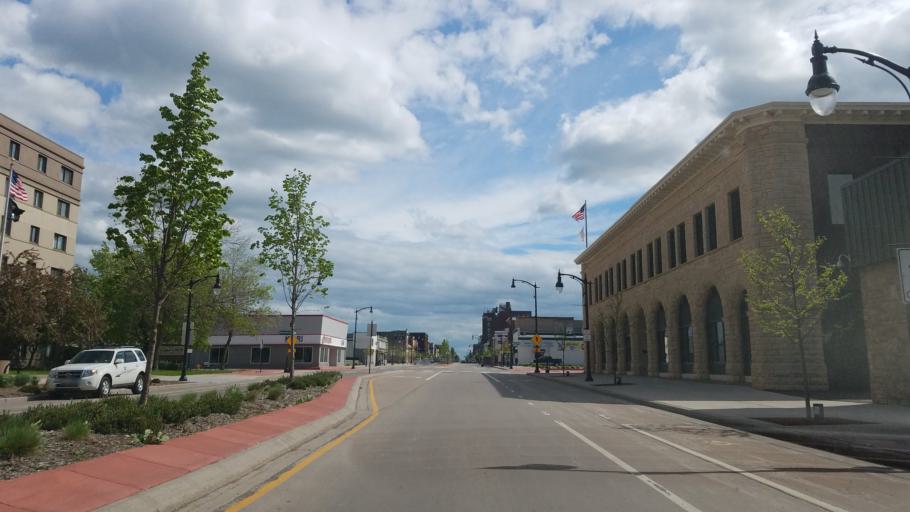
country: US
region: Wisconsin
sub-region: Douglas County
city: Superior
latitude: 46.7275
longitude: -92.1039
